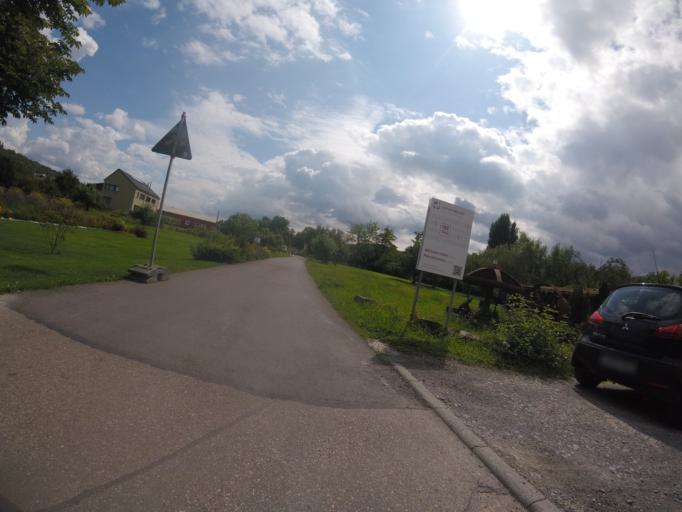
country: DE
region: Baden-Wuerttemberg
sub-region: Regierungsbezirk Stuttgart
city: Winterbach
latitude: 48.8079
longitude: 9.4355
